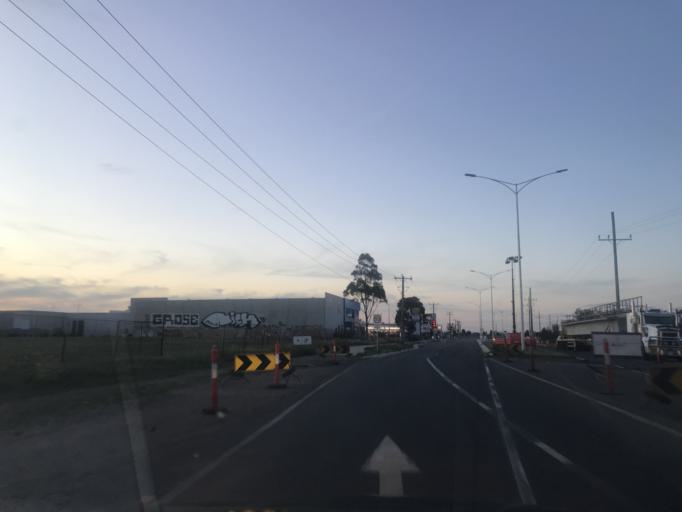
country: AU
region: Victoria
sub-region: Wyndham
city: Williams Landing
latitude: -37.8663
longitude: 144.7338
